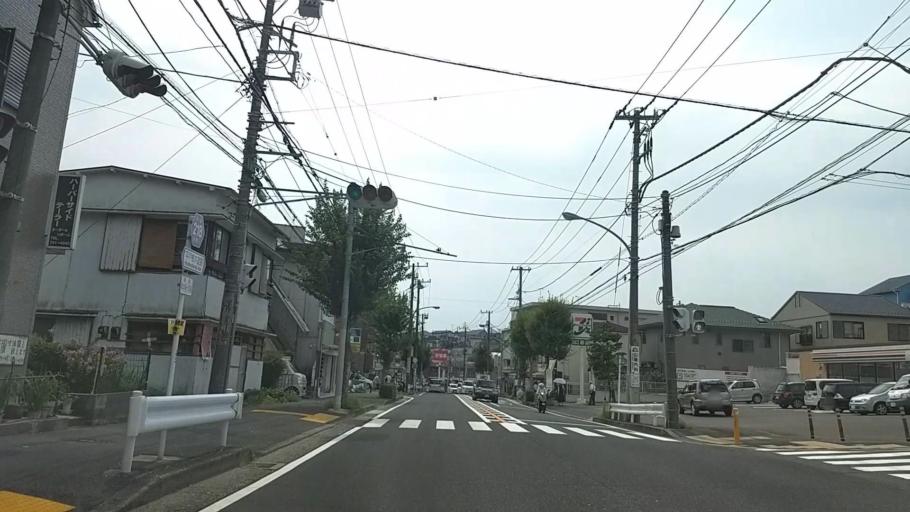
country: JP
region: Kanagawa
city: Yokohama
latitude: 35.4247
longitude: 139.5843
